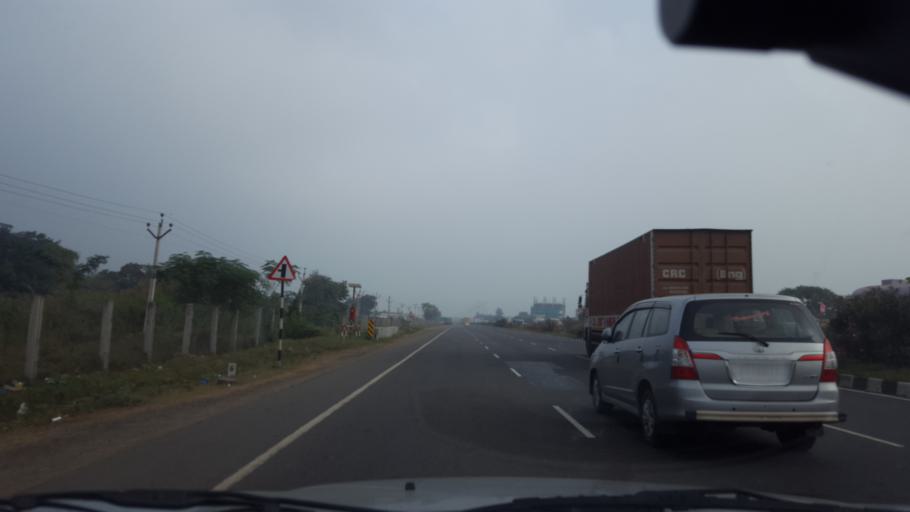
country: IN
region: Andhra Pradesh
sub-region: Prakasam
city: Addanki
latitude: 15.6810
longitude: 80.0176
